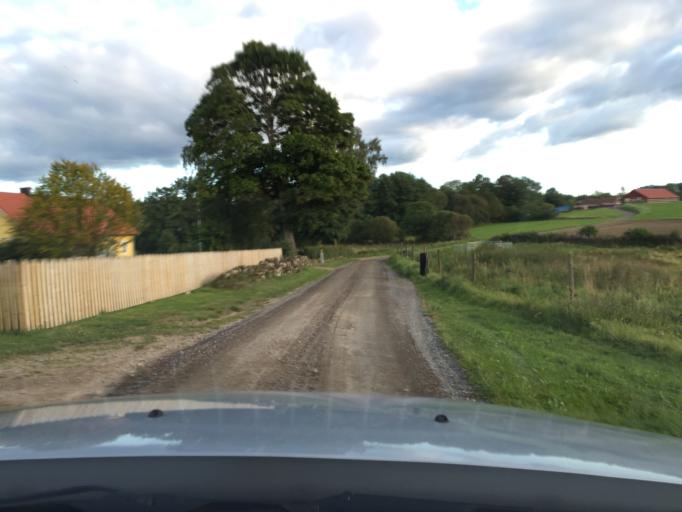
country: SE
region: Skane
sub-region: Hassleholms Kommun
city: Sosdala
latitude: 56.0405
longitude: 13.7099
